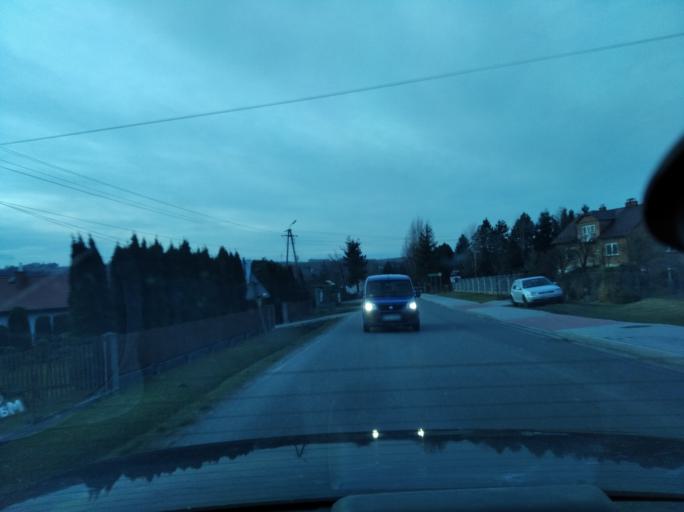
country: PL
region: Subcarpathian Voivodeship
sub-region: Powiat ropczycko-sedziszowski
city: Iwierzyce
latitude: 50.0040
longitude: 21.7549
